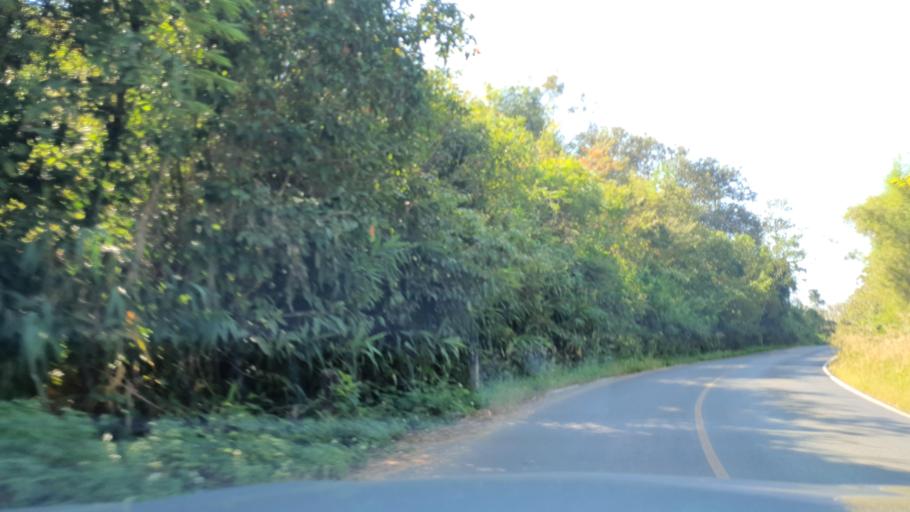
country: TH
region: Nan
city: Pua
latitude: 19.1118
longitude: 100.9089
